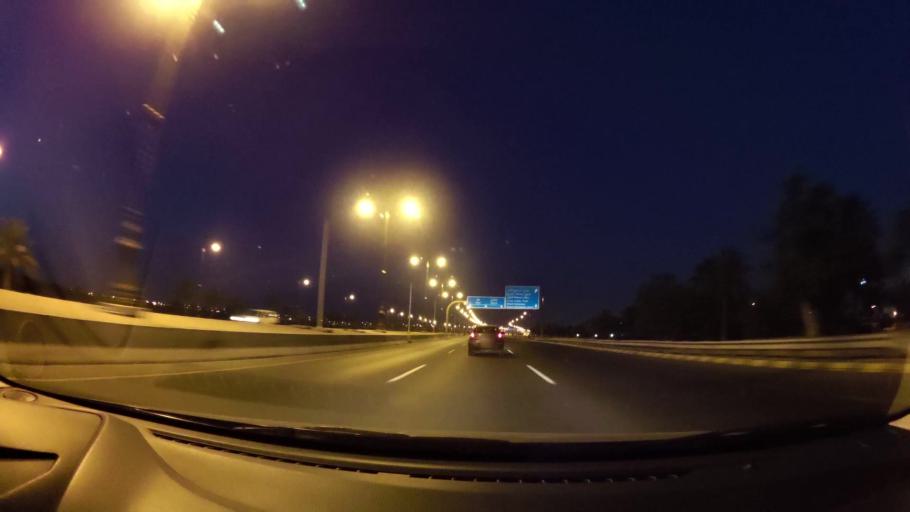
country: OM
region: Muhafazat Masqat
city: Bawshar
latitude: 23.5905
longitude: 58.3219
